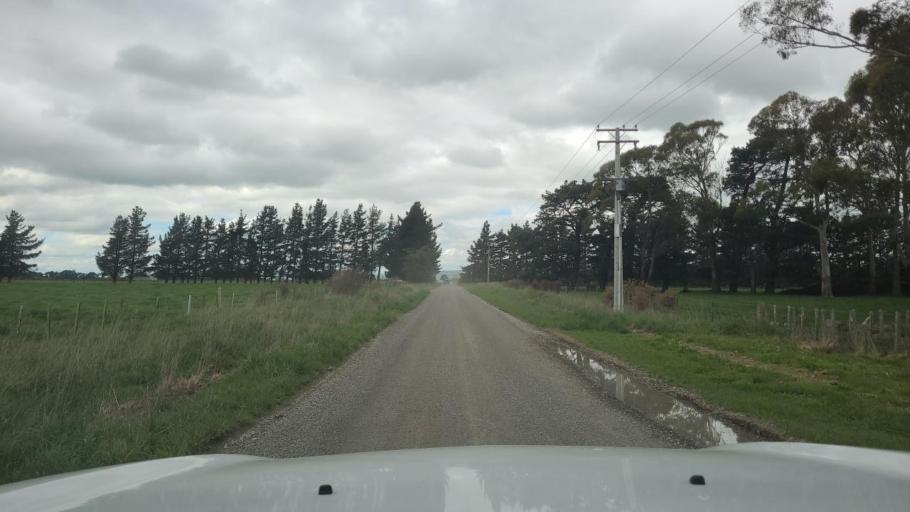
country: NZ
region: Wellington
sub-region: Masterton District
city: Masterton
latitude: -41.1187
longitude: 175.3907
